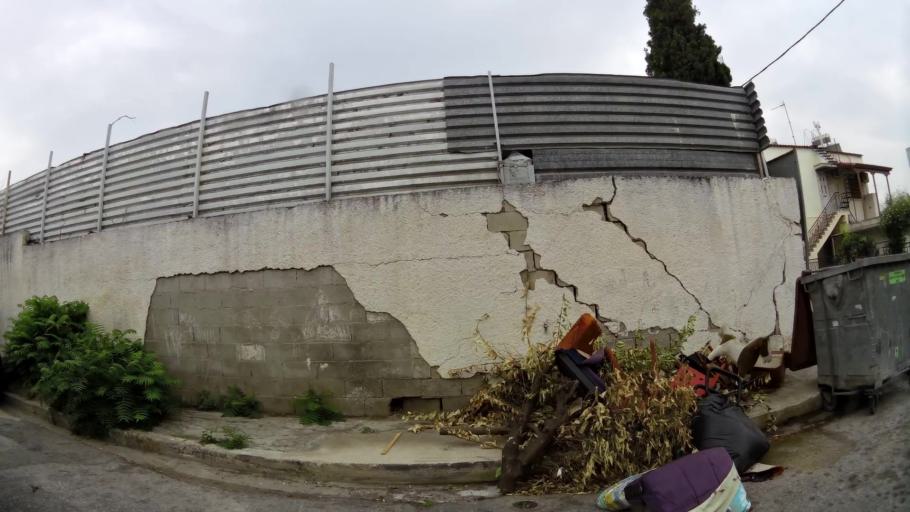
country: GR
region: Attica
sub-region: Nomos Piraios
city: Agios Ioannis Rentis
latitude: 37.9683
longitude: 23.6645
